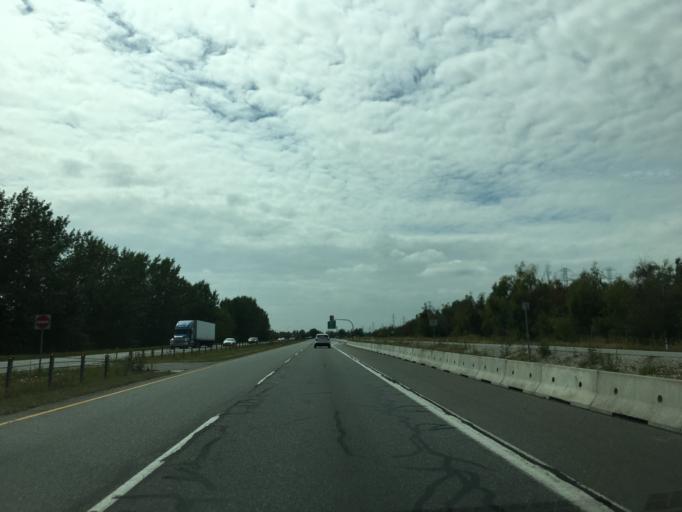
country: CA
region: British Columbia
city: Ladner
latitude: 49.0905
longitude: -122.9947
